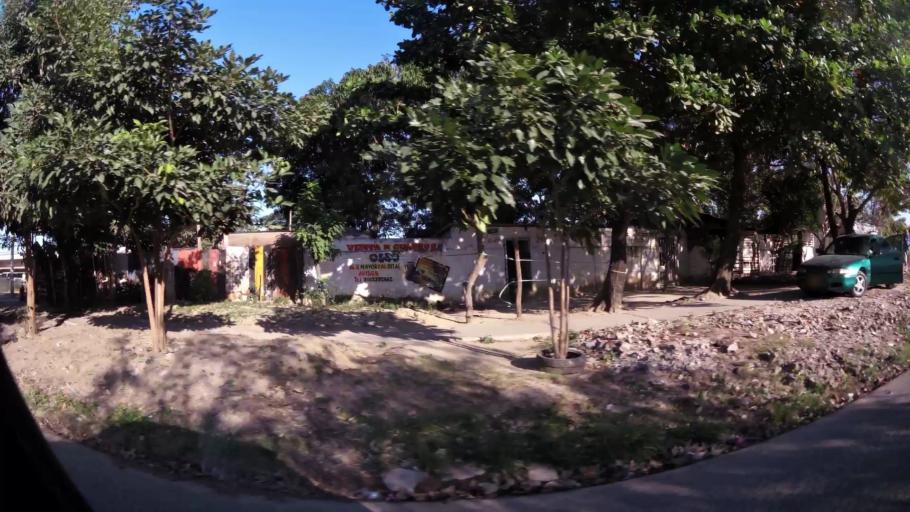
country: CO
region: Atlantico
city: Soledad
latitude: 10.9229
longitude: -74.8000
